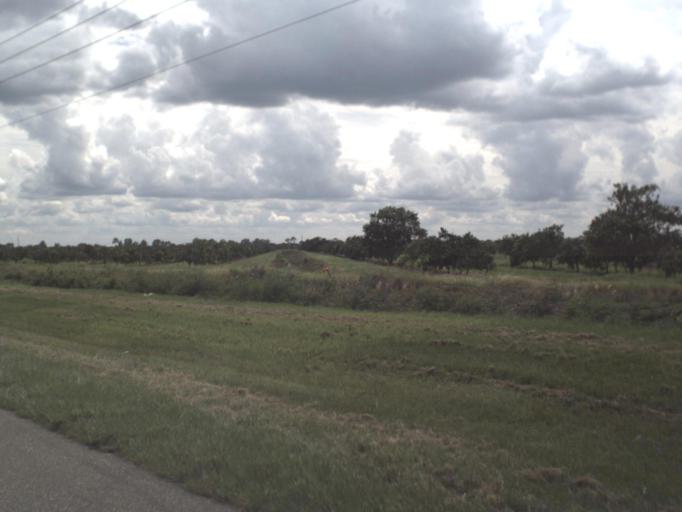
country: US
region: Florida
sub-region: DeSoto County
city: Nocatee
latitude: 27.0318
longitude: -81.7702
